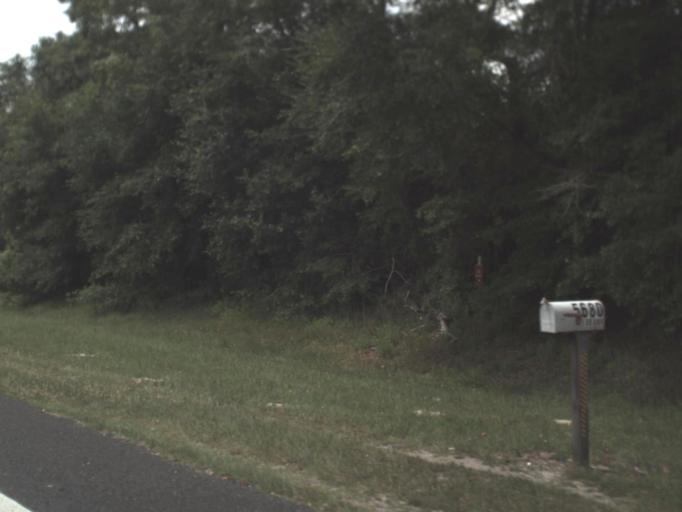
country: US
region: Florida
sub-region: Clay County
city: Green Cove Springs
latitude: 29.8891
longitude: -81.6685
